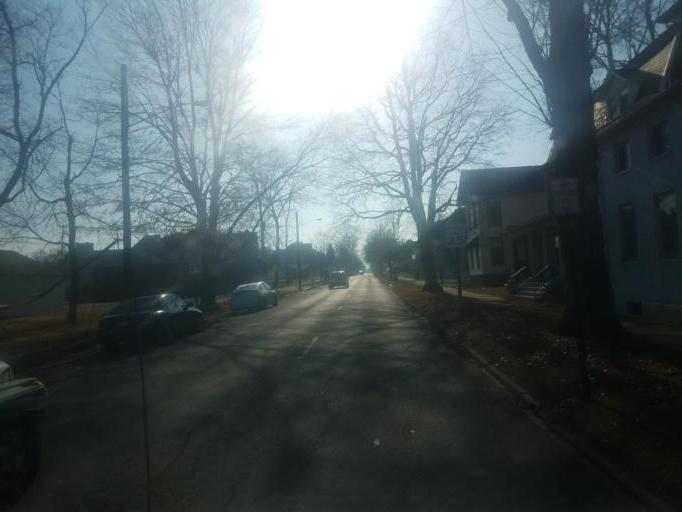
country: US
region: Ohio
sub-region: Seneca County
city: Tiffin
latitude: 41.1132
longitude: -83.1780
